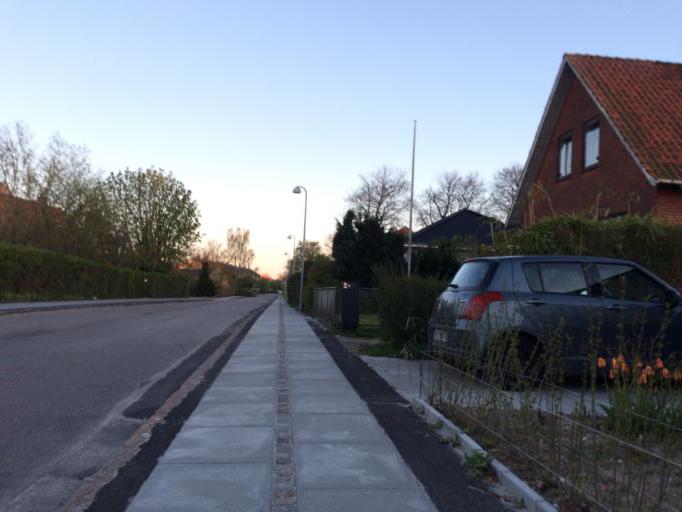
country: DK
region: Capital Region
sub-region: Hoje-Taastrup Kommune
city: Taastrup
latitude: 55.6479
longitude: 12.2929
